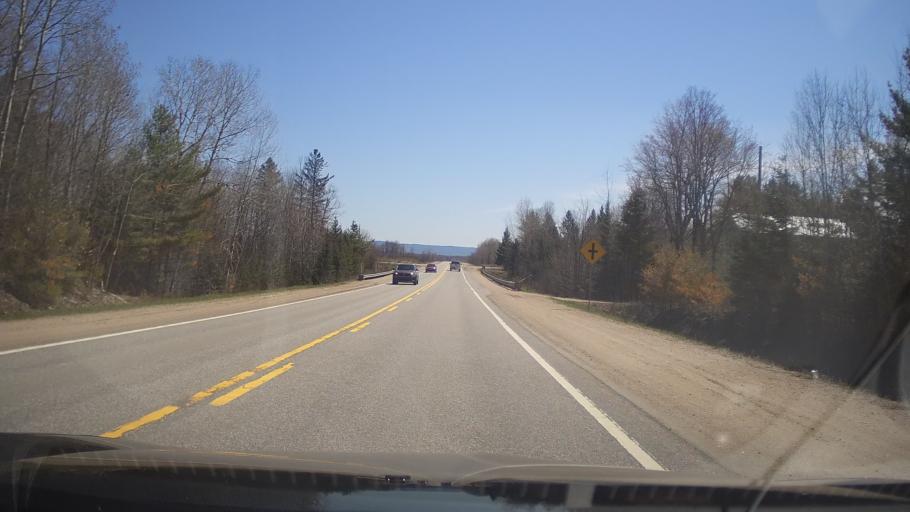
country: CA
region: Ontario
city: Arnprior
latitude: 45.5247
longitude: -76.2877
